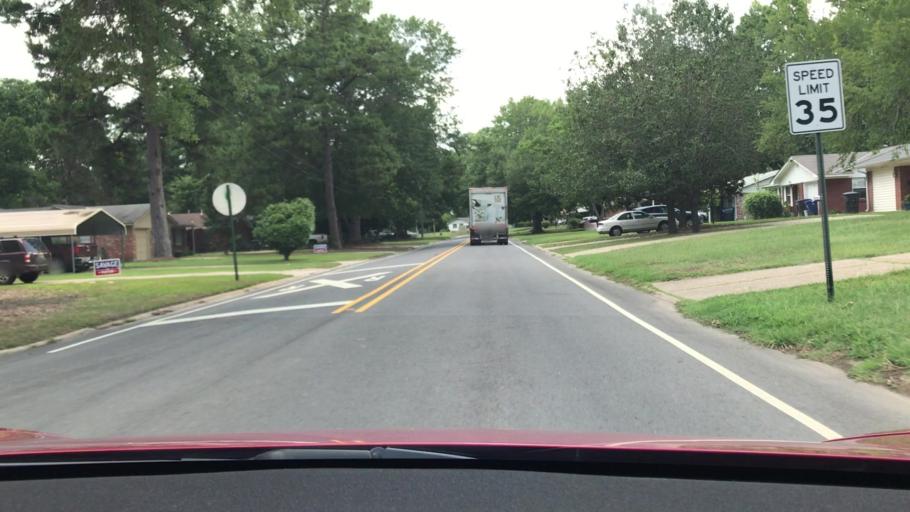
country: US
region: Louisiana
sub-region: De Soto Parish
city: Stonewall
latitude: 32.3952
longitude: -93.8005
